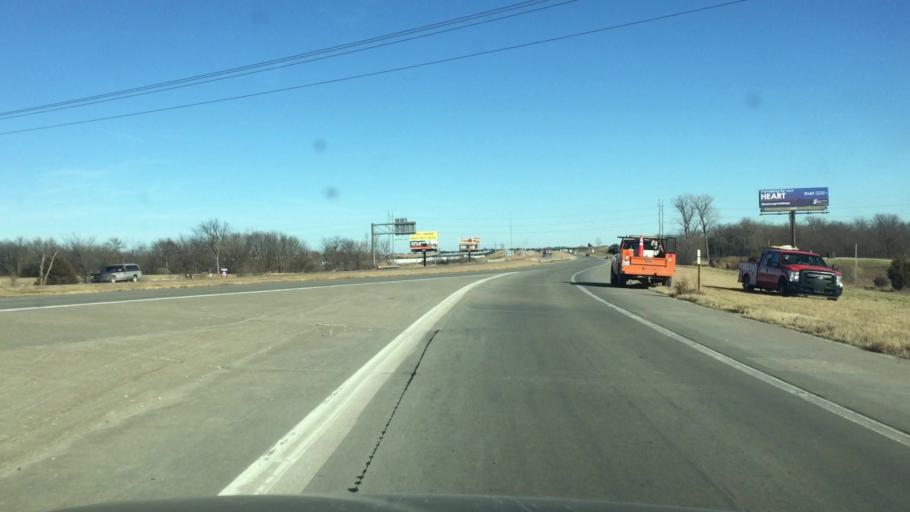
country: US
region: Kansas
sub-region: Franklin County
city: Ottawa
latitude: 38.5765
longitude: -95.2638
